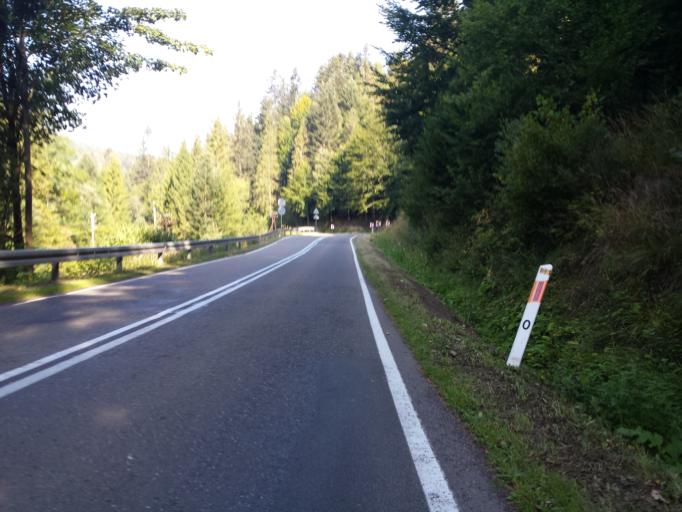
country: PL
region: Subcarpathian Voivodeship
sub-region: Powiat leski
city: Cisna
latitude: 49.2239
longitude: 22.3106
